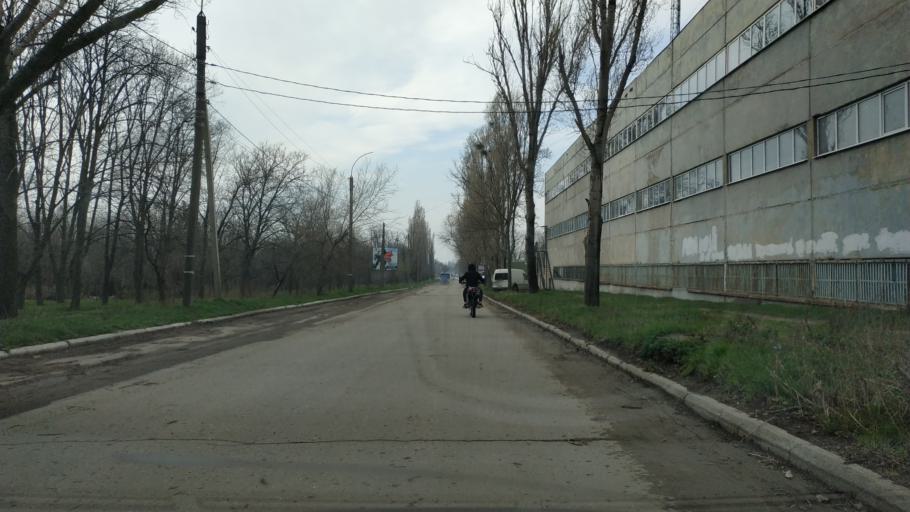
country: MD
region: Cahul
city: Cahul
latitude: 45.8909
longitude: 28.1984
